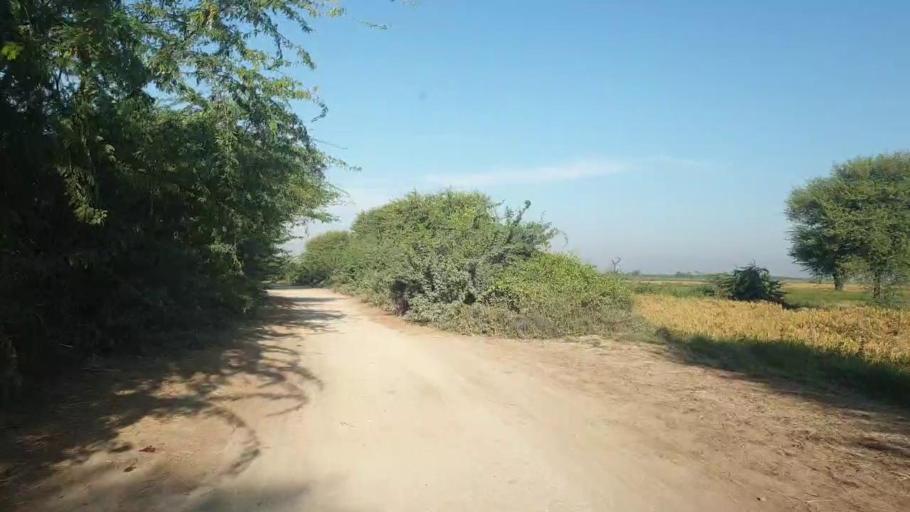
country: PK
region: Sindh
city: Talhar
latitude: 24.8246
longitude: 68.8390
